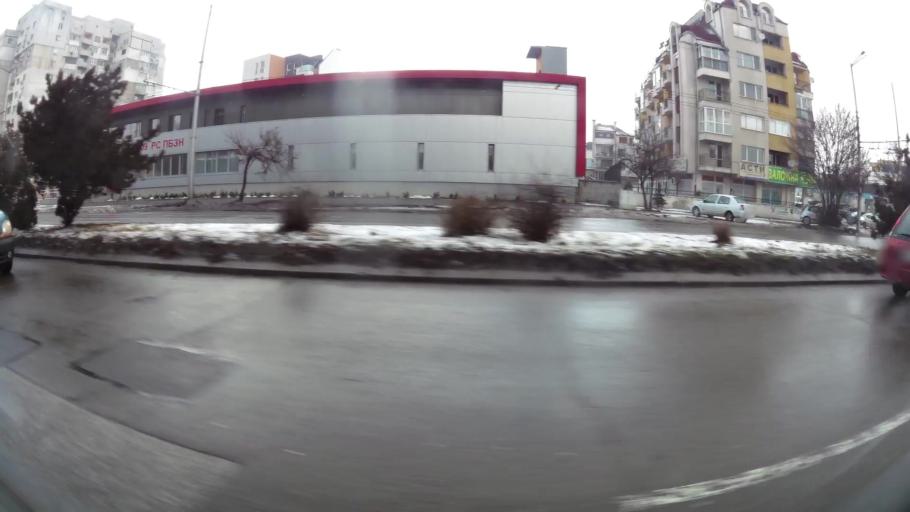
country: BG
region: Sofia-Capital
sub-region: Stolichna Obshtina
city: Sofia
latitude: 42.7163
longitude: 23.2777
